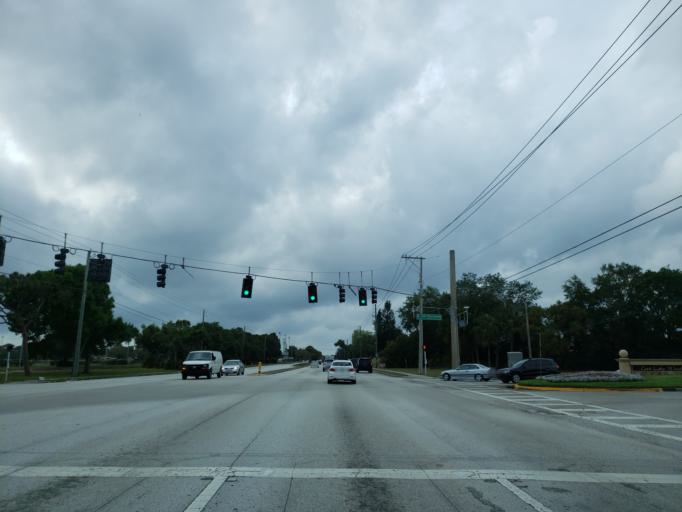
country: US
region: Florida
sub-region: Pinellas County
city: Saint George
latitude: 28.0529
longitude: -82.6997
